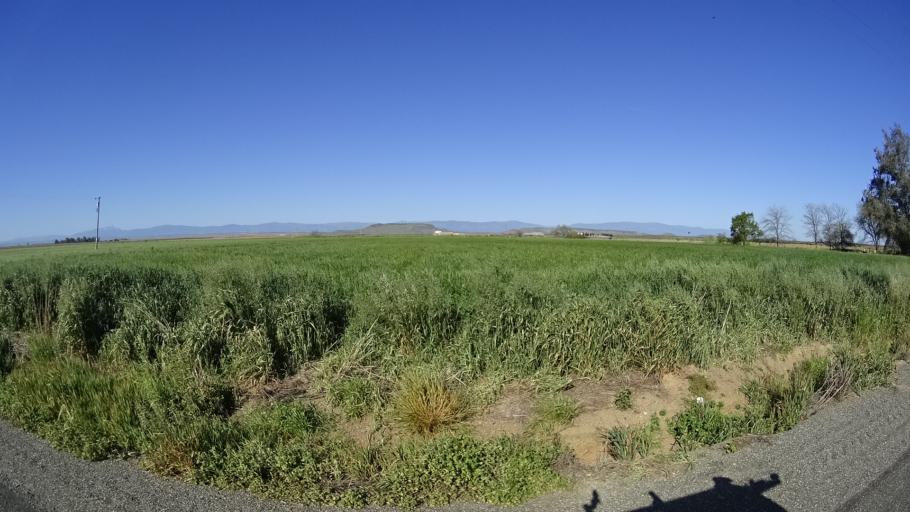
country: US
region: California
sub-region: Glenn County
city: Orland
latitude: 39.7543
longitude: -122.2479
